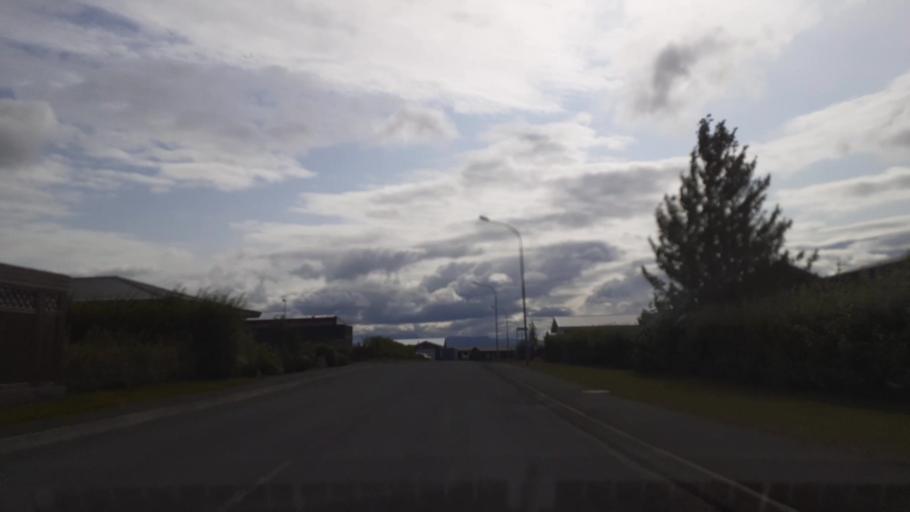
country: IS
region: South
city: Vestmannaeyjar
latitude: 63.8338
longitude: -20.3896
